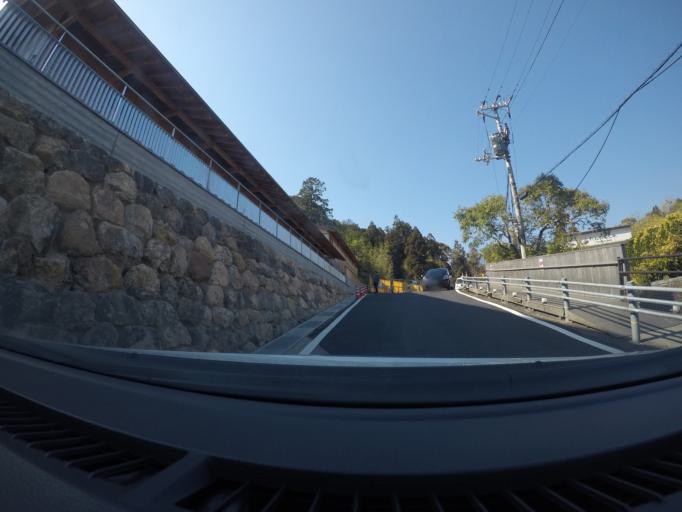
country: JP
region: Kochi
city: Kochi-shi
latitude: 33.5467
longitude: 133.5777
